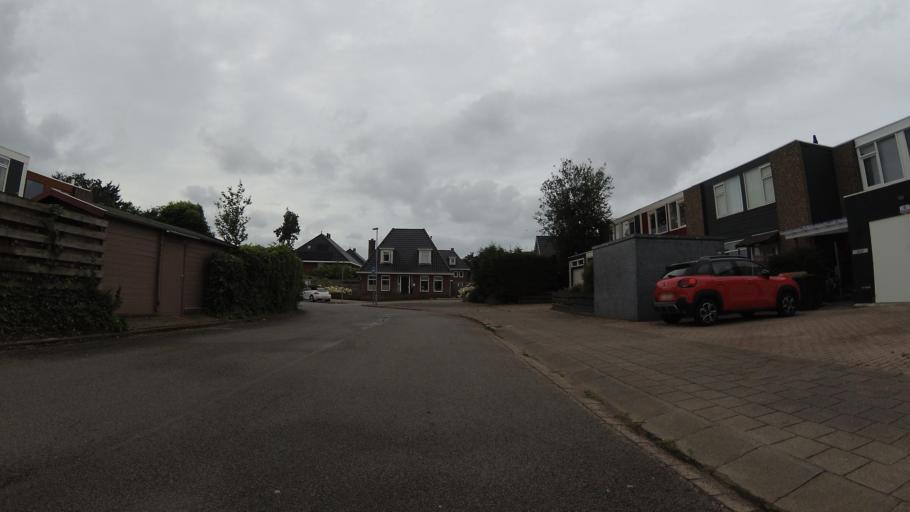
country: NL
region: North Holland
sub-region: Gemeente Den Helder
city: Den Helder
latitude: 52.8980
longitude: 4.7458
